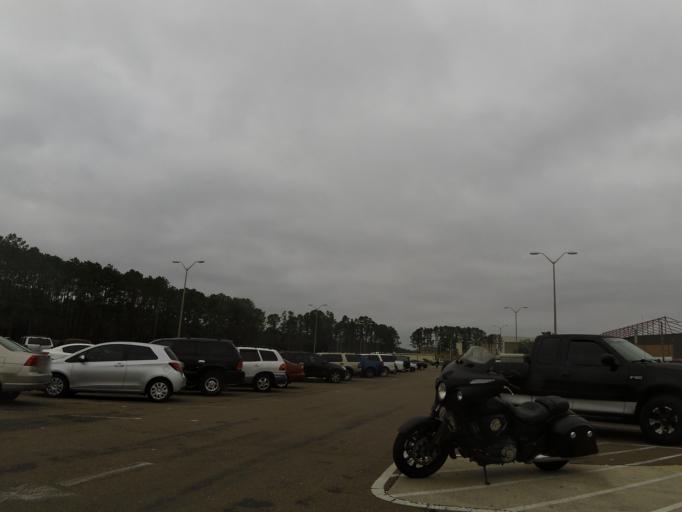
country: US
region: Florida
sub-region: Duval County
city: Baldwin
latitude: 30.2315
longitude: -81.8816
